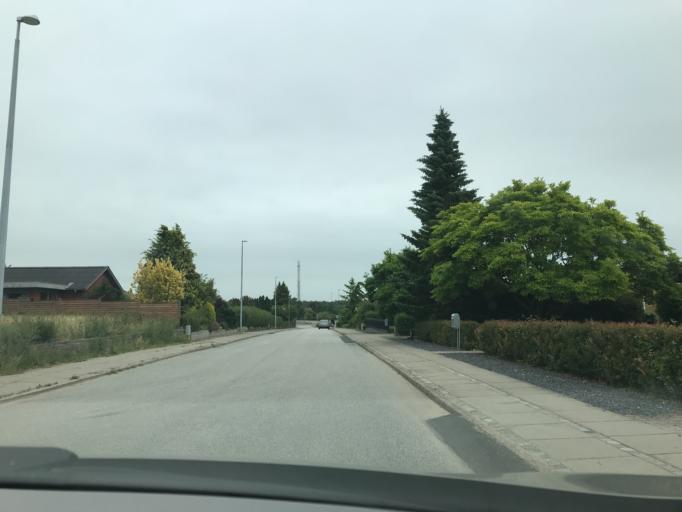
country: DK
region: South Denmark
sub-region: Middelfart Kommune
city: Middelfart
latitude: 55.4954
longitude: 9.7392
